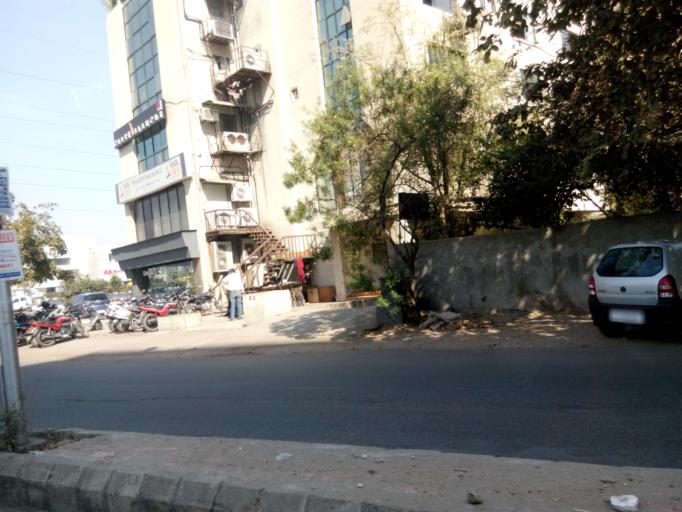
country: IN
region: Gujarat
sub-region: Ahmadabad
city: Sarkhej
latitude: 23.0321
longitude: 72.5104
